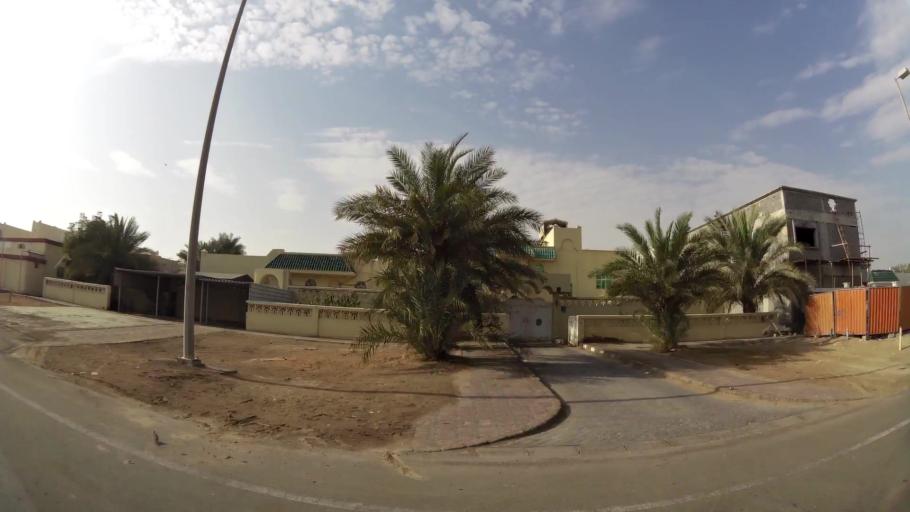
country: AE
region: Abu Dhabi
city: Abu Dhabi
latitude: 24.2614
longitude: 54.6717
